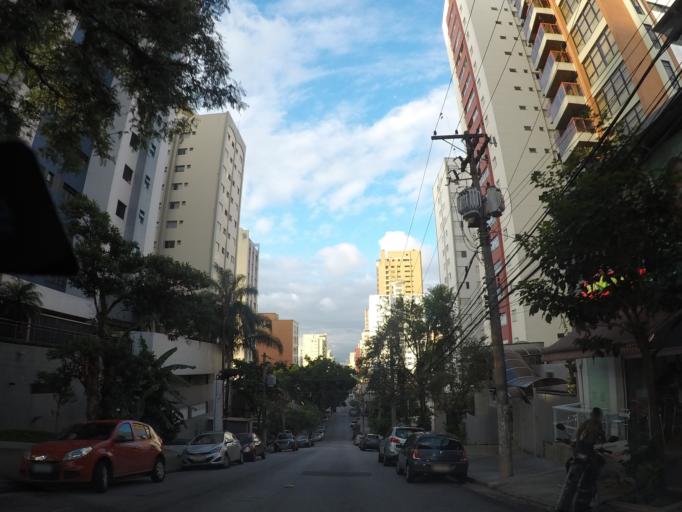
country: BR
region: Sao Paulo
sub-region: Sao Paulo
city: Sao Paulo
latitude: -23.5393
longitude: -46.6815
